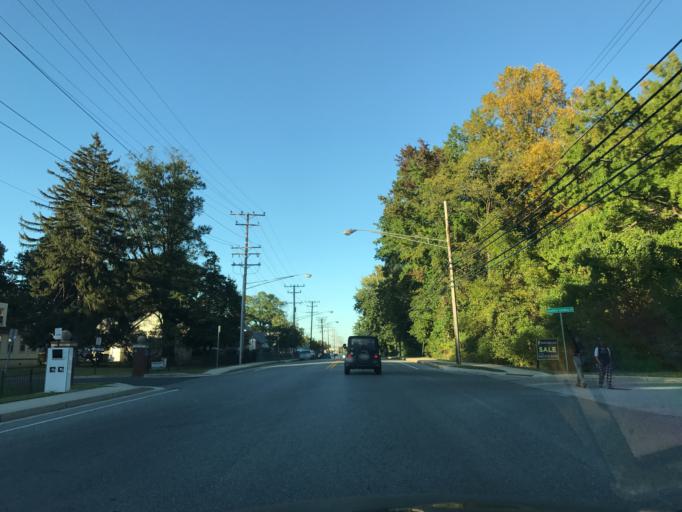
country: US
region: Maryland
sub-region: Baltimore County
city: Middle River
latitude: 39.3201
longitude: -76.4478
